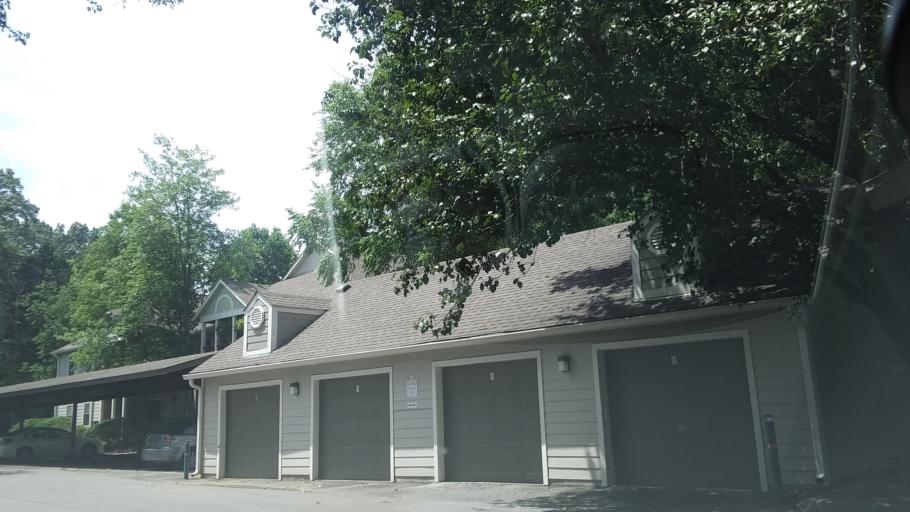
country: US
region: Tennessee
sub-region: Rutherford County
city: La Vergne
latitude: 36.0938
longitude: -86.6463
